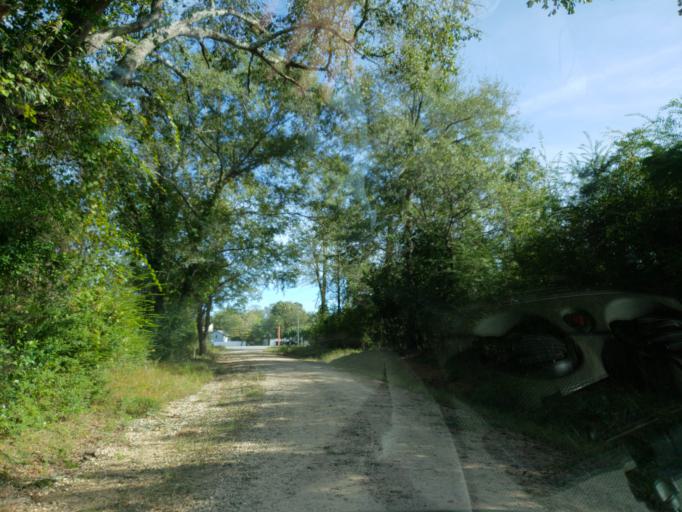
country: US
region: Georgia
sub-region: Crawford County
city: Roberta
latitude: 32.7234
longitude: -84.0133
